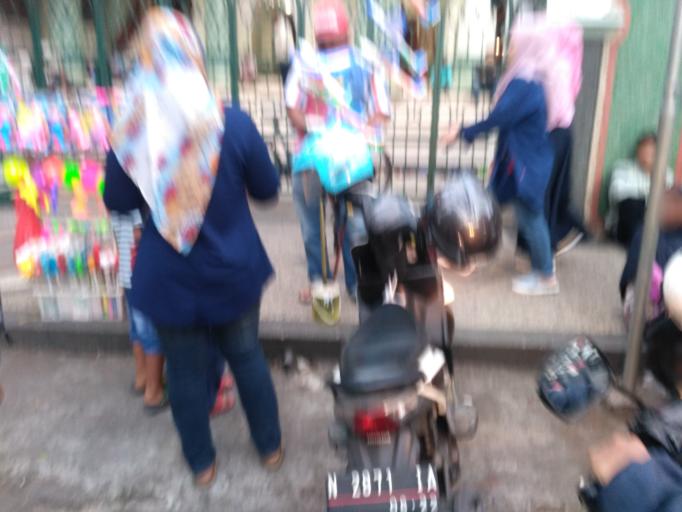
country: ID
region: East Java
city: Malang
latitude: -7.9826
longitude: 112.6301
